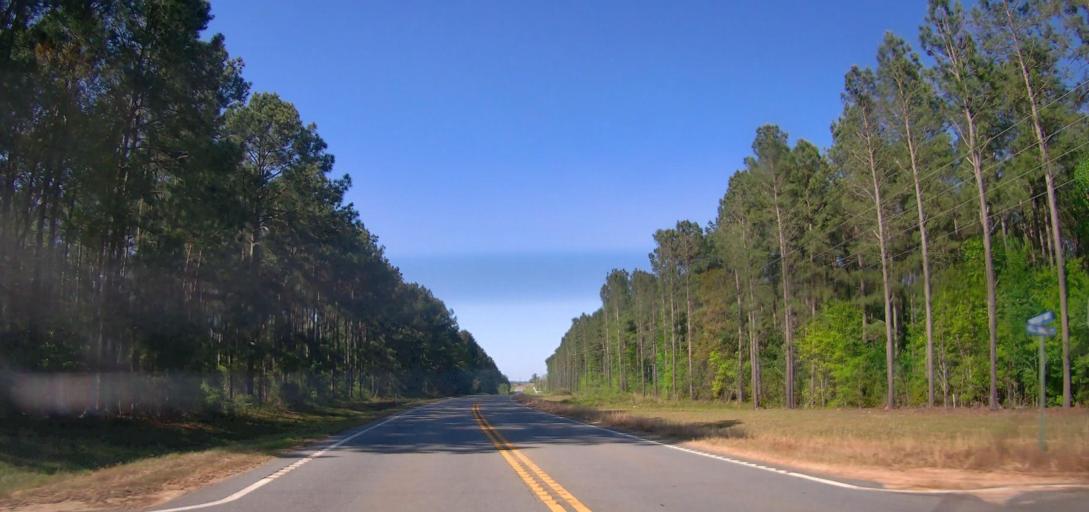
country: US
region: Georgia
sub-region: Pulaski County
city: Hawkinsville
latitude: 32.1666
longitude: -83.5119
